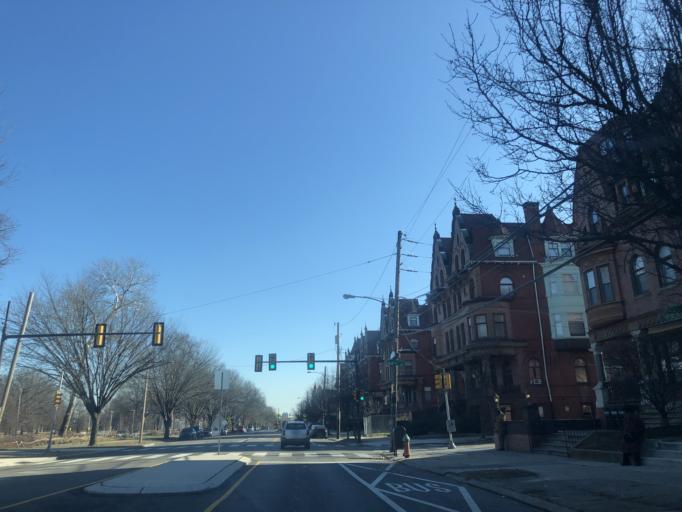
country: US
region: Pennsylvania
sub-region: Montgomery County
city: Bala-Cynwyd
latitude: 39.9765
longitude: -75.2095
